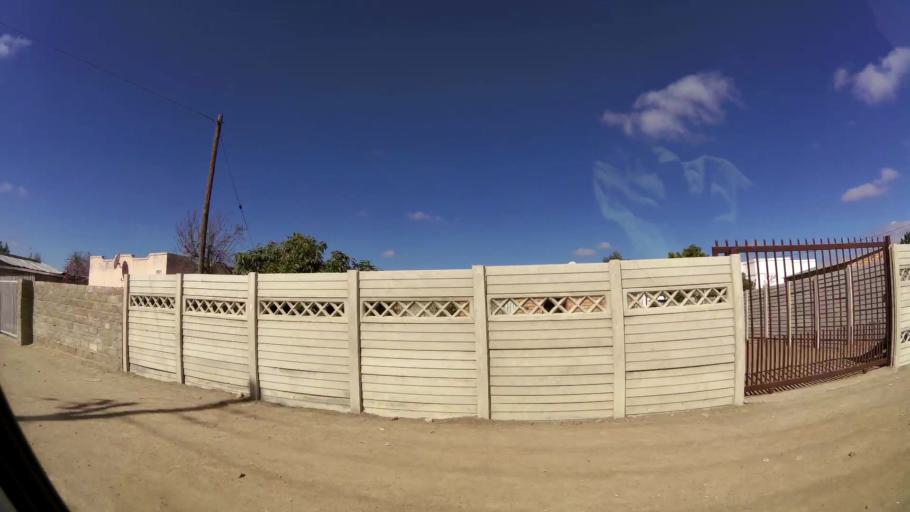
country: ZA
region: Limpopo
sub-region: Capricorn District Municipality
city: Polokwane
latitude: -23.8559
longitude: 29.3991
